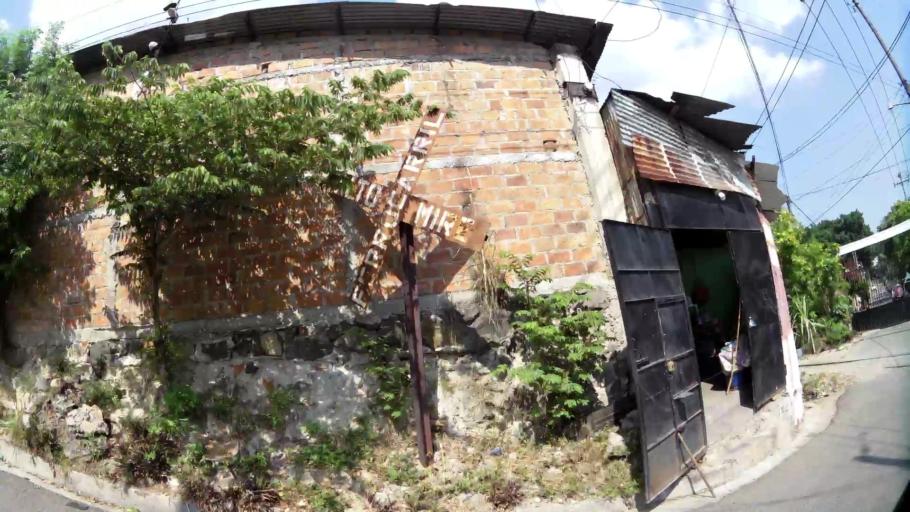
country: SV
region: San Salvador
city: Delgado
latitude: 13.7121
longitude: -89.1701
